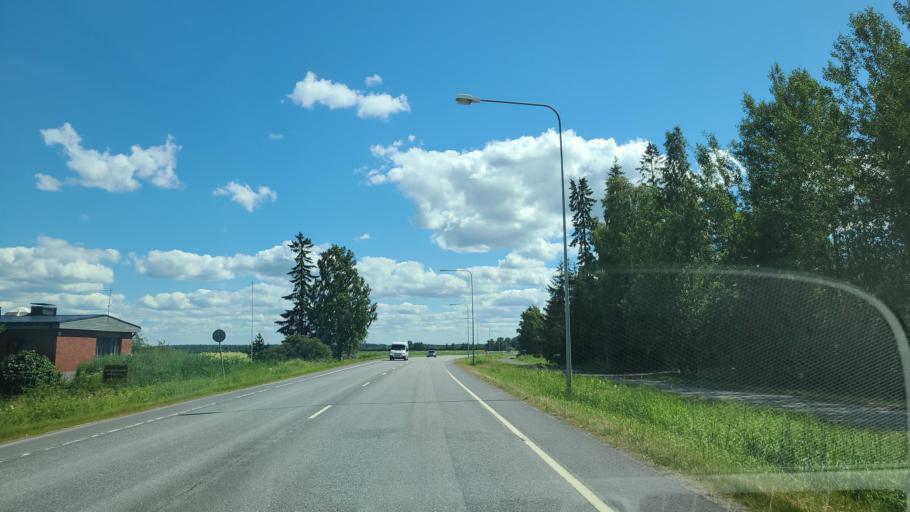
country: FI
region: Southern Ostrobothnia
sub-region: Seinaejoki
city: Seinaejoki
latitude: 62.8581
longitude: 22.7620
